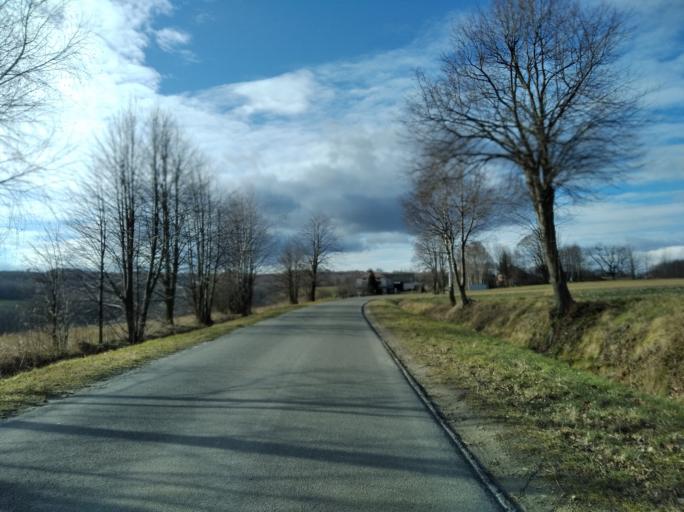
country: PL
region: Subcarpathian Voivodeship
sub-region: Powiat strzyzowski
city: Wisniowa
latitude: 49.9173
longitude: 21.6574
